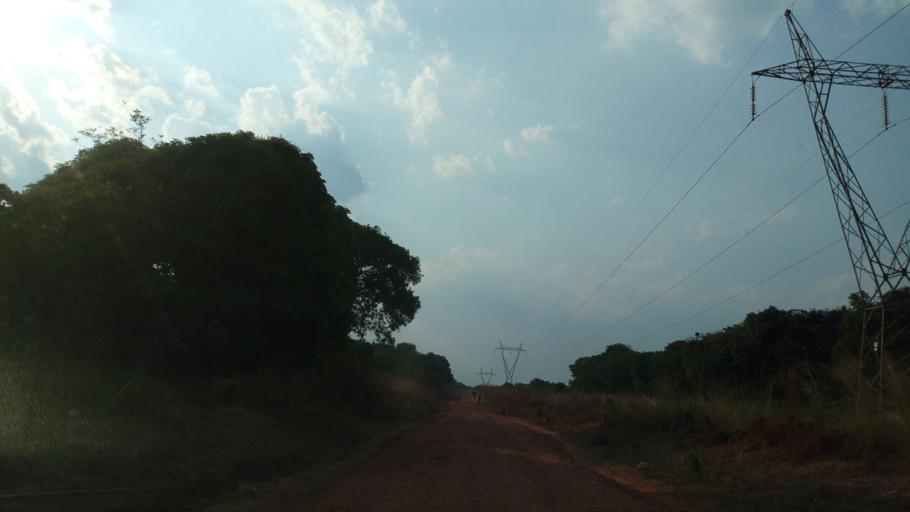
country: TZ
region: Kigoma
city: Kigoma
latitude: -5.1355
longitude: 28.9086
